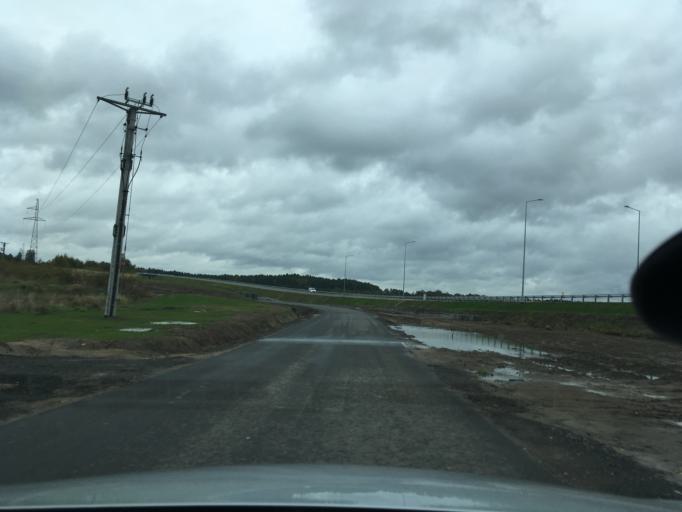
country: PL
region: Pomeranian Voivodeship
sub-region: Powiat koscierski
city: Koscierzyna
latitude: 54.1117
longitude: 17.9989
